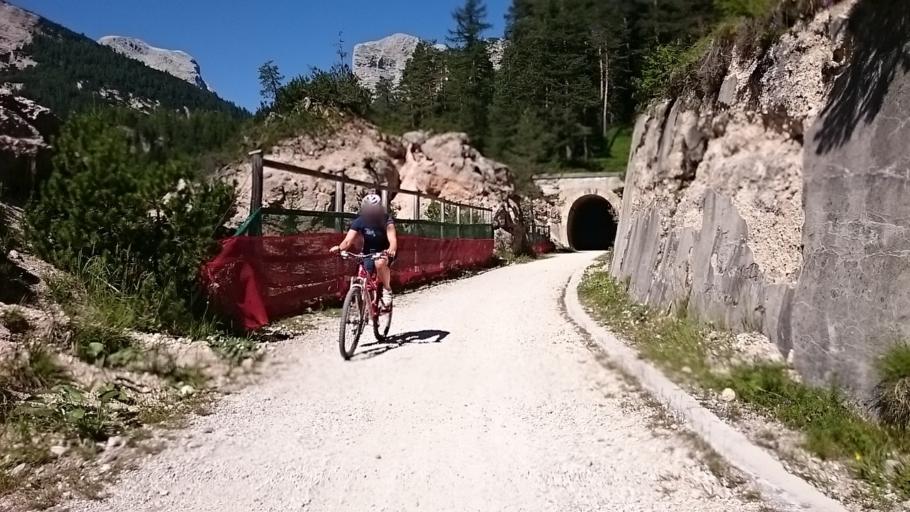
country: IT
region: Veneto
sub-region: Provincia di Belluno
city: Cortina d'Ampezzo
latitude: 46.5981
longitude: 12.1199
